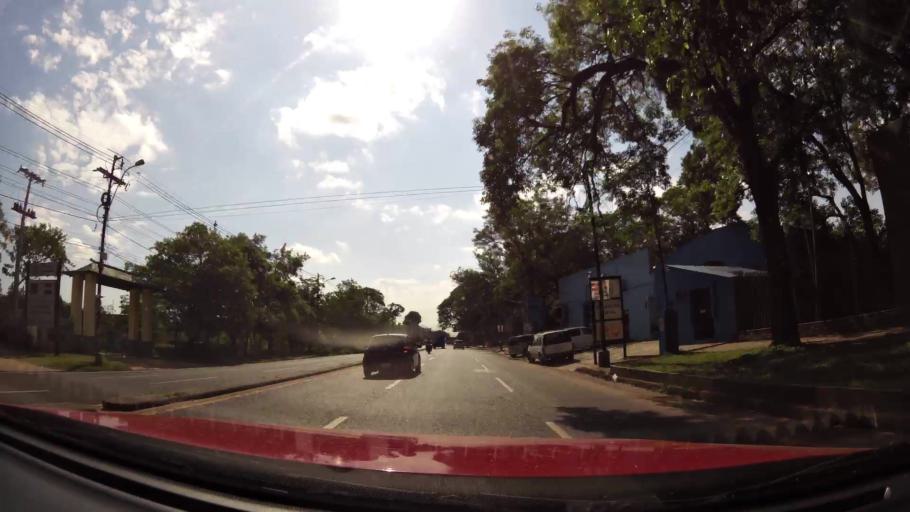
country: PY
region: Central
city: Fernando de la Mora
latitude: -25.3381
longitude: -57.5255
